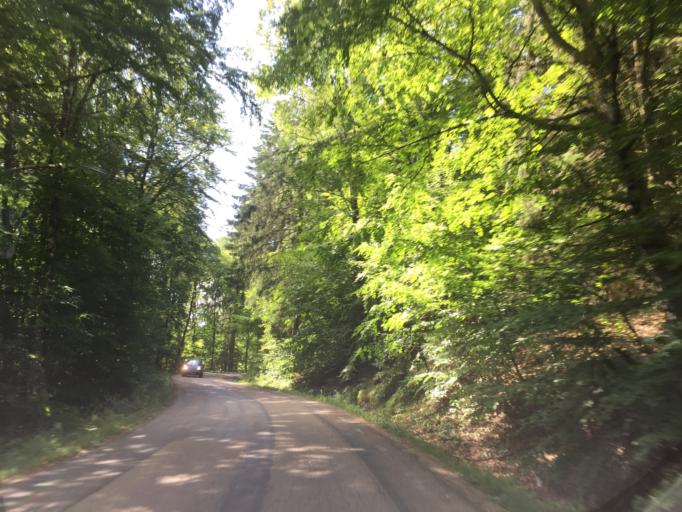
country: SE
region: Vaestra Goetaland
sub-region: Orust
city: Henan
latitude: 58.3037
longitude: 11.6618
